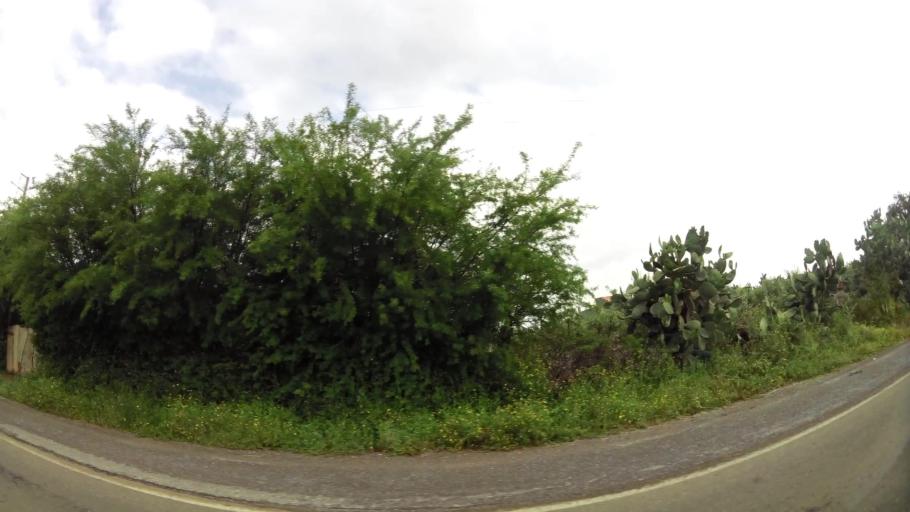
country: MA
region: Rabat-Sale-Zemmour-Zaer
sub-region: Khemisset
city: Khemisset
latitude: 33.7780
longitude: -6.1373
